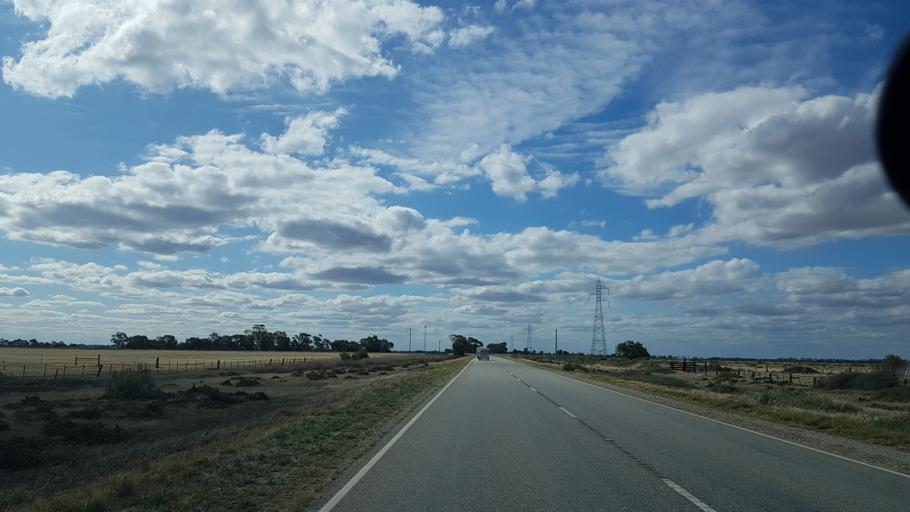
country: AU
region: Victoria
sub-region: Swan Hill
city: Swan Hill
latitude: -35.8852
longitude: 143.9411
